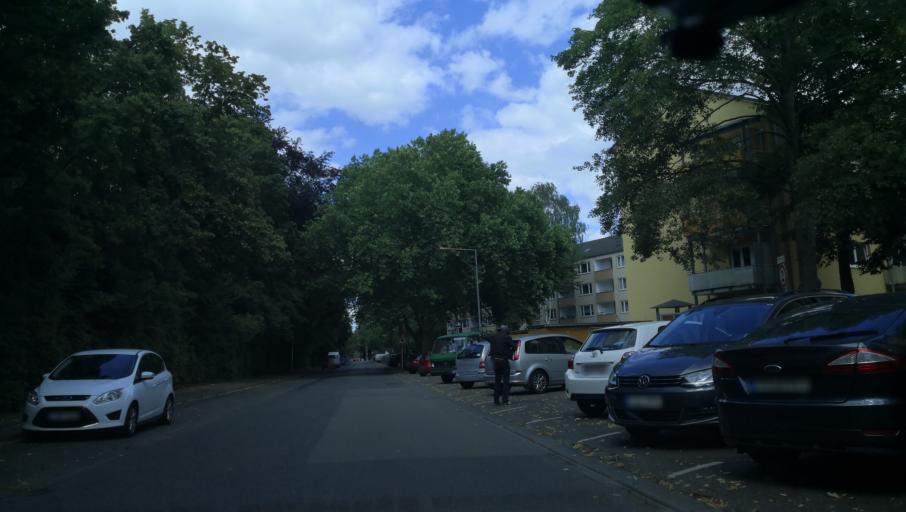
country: DE
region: North Rhine-Westphalia
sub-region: Regierungsbezirk Koln
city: Mengenich
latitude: 50.9674
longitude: 6.8823
